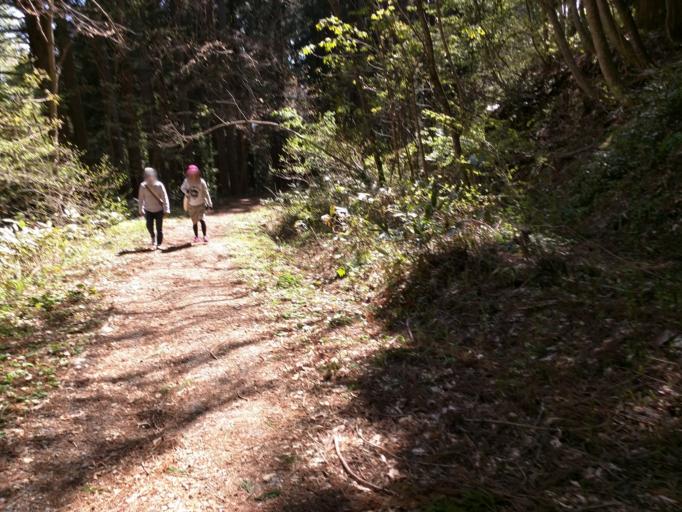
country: JP
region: Nagano
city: Nagano-shi
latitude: 36.7327
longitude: 138.0769
